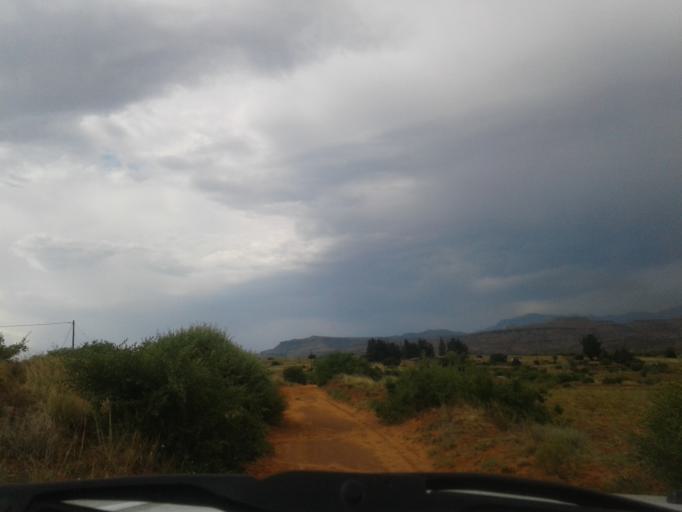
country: LS
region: Quthing
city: Quthing
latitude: -30.3820
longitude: 27.5546
